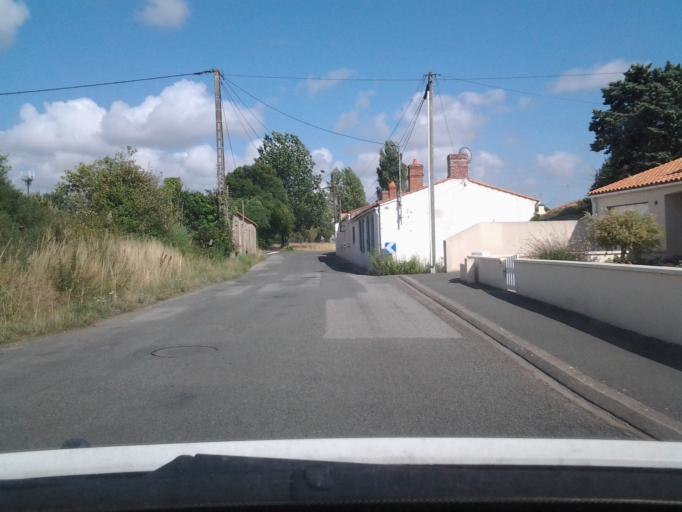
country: FR
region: Pays de la Loire
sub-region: Departement de la Vendee
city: Olonne-sur-Mer
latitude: 46.5363
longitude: -1.7654
